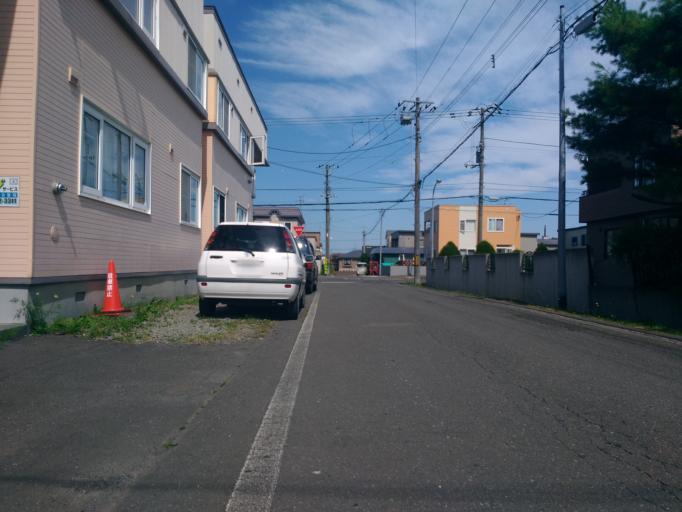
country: JP
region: Hokkaido
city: Ebetsu
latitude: 43.0813
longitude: 141.5078
